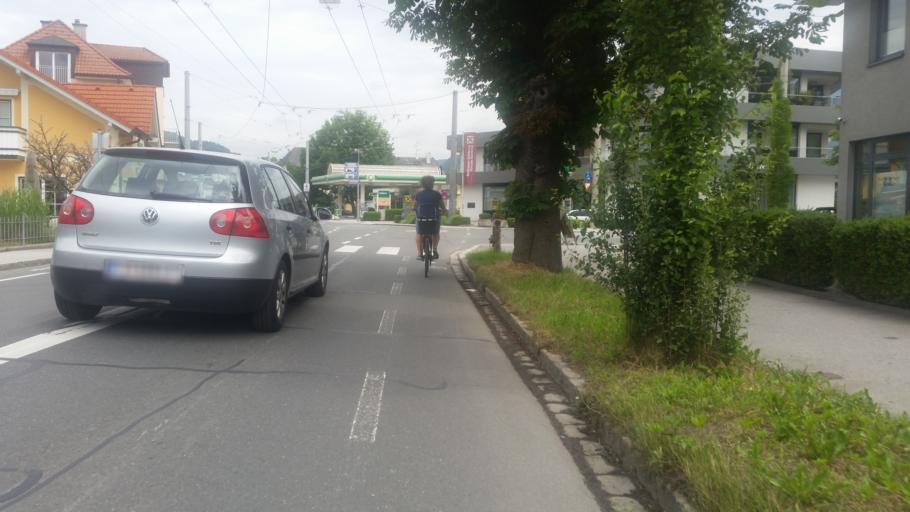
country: AT
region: Salzburg
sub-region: Salzburg Stadt
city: Salzburg
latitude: 47.7837
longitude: 13.0518
